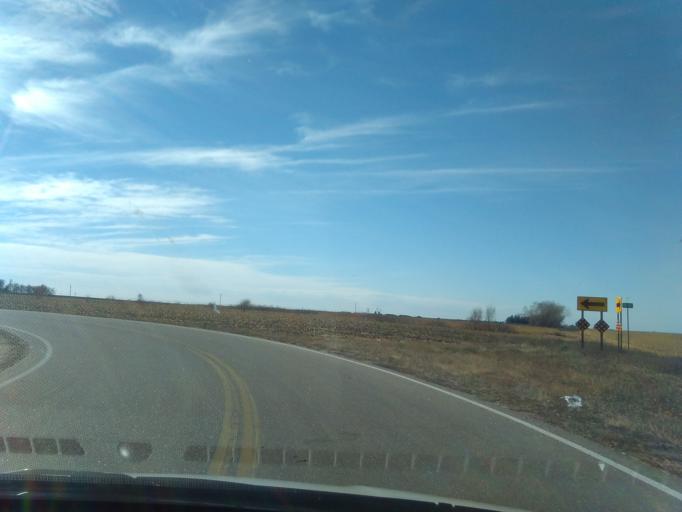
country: US
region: Nebraska
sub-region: Adams County
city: Hastings
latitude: 40.5100
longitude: -98.2507
